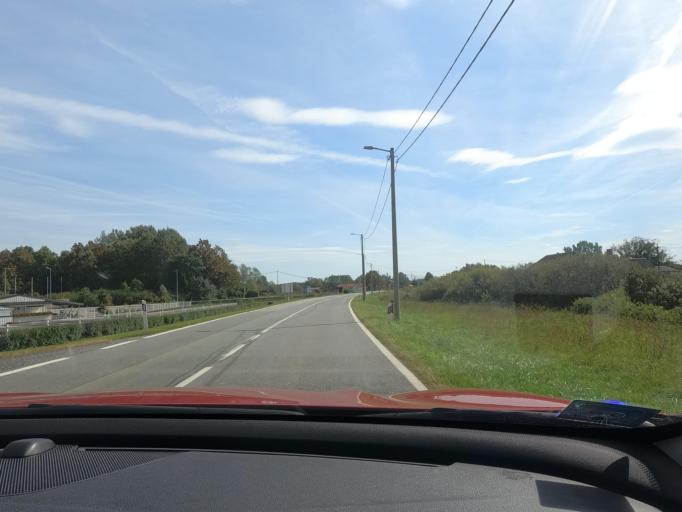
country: HR
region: Sisacko-Moslavacka
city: Budasevo
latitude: 45.4908
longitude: 16.4537
